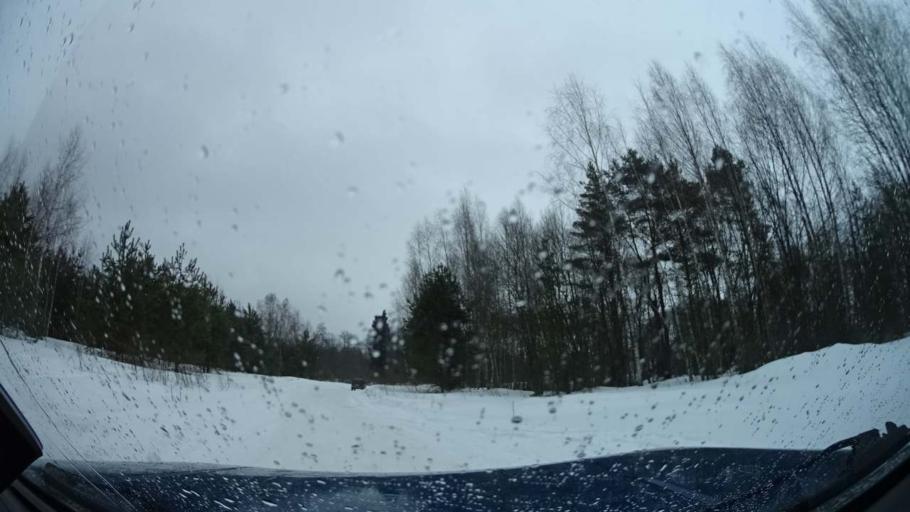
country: RU
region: Tverskaya
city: Konakovo
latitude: 56.7059
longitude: 36.7130
